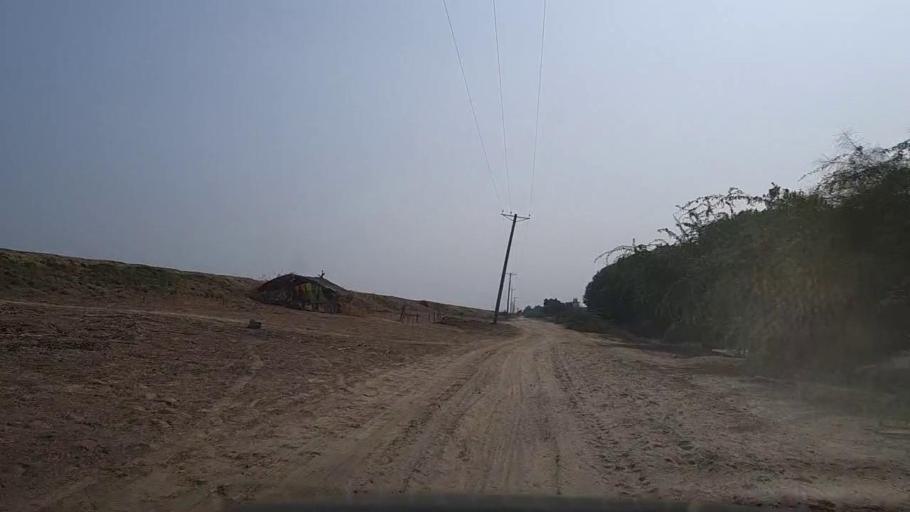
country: PK
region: Sindh
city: Thatta
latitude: 24.5602
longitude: 67.9144
